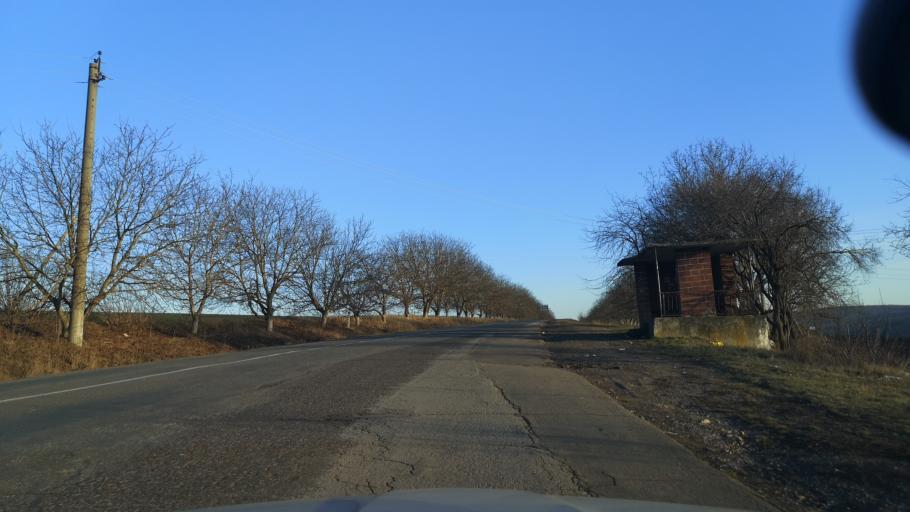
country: MD
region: Orhei
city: Orhei
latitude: 47.2919
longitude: 28.8108
